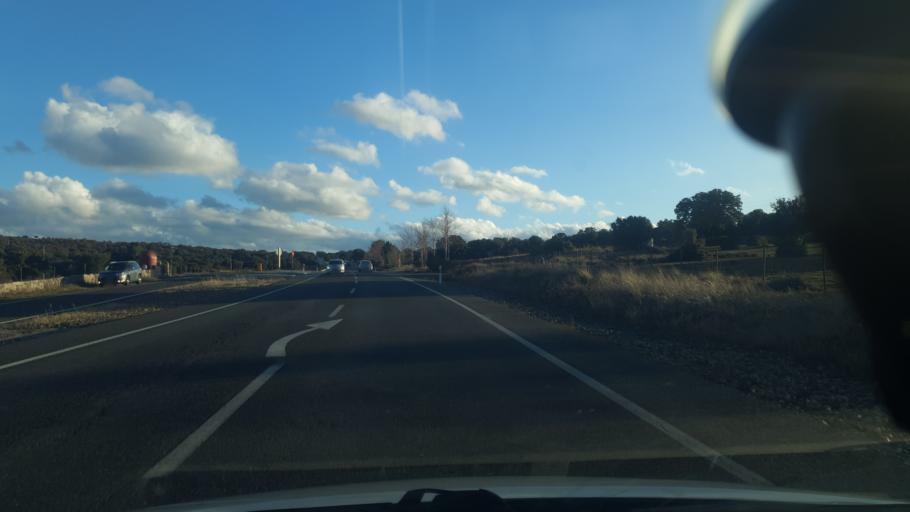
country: ES
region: Castille and Leon
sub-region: Provincia de Avila
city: Mingorria
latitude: 40.7249
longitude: -4.6746
